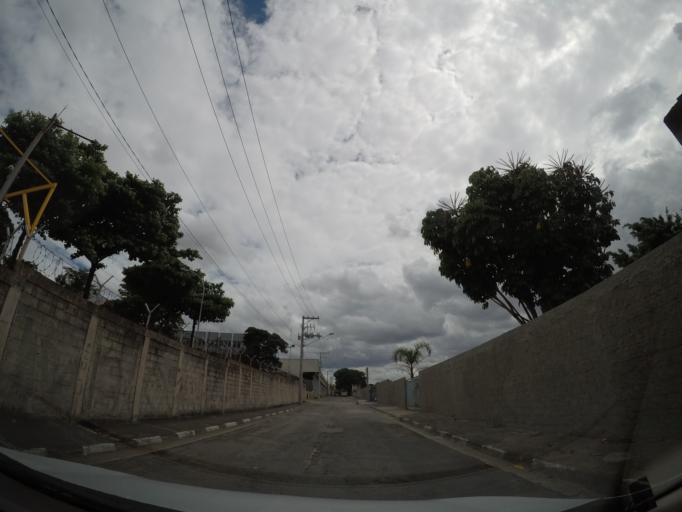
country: BR
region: Sao Paulo
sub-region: Guarulhos
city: Guarulhos
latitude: -23.4920
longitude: -46.5573
